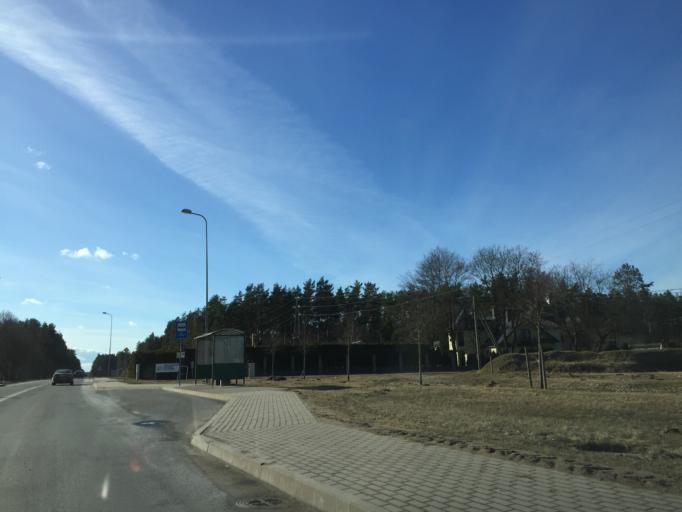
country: LV
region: Stopini
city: Ulbroka
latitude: 56.9468
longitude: 24.3523
